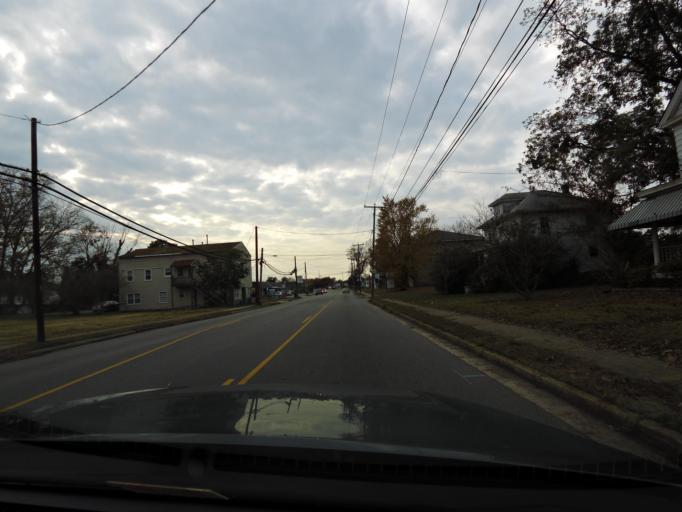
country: US
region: Virginia
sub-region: City of Hampton
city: East Hampton
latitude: 37.0331
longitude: -76.3331
